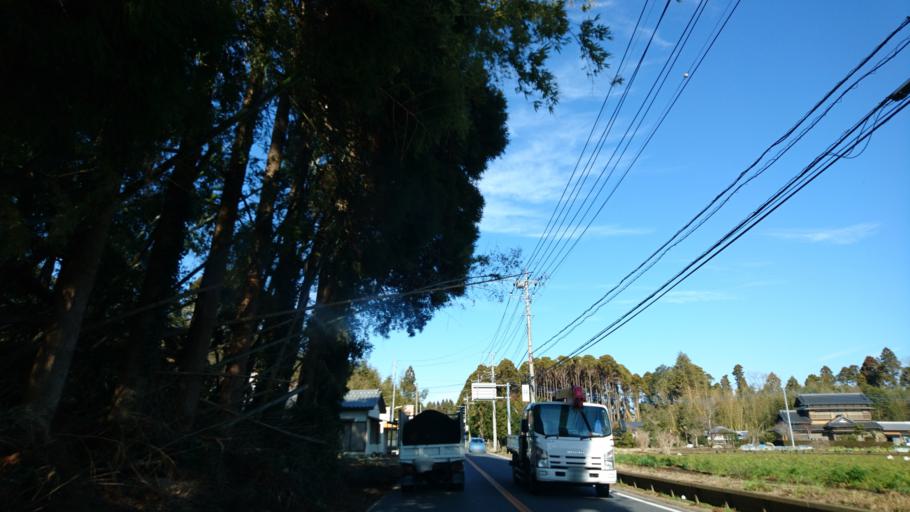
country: JP
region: Chiba
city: Yachimata
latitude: 35.6157
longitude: 140.3204
